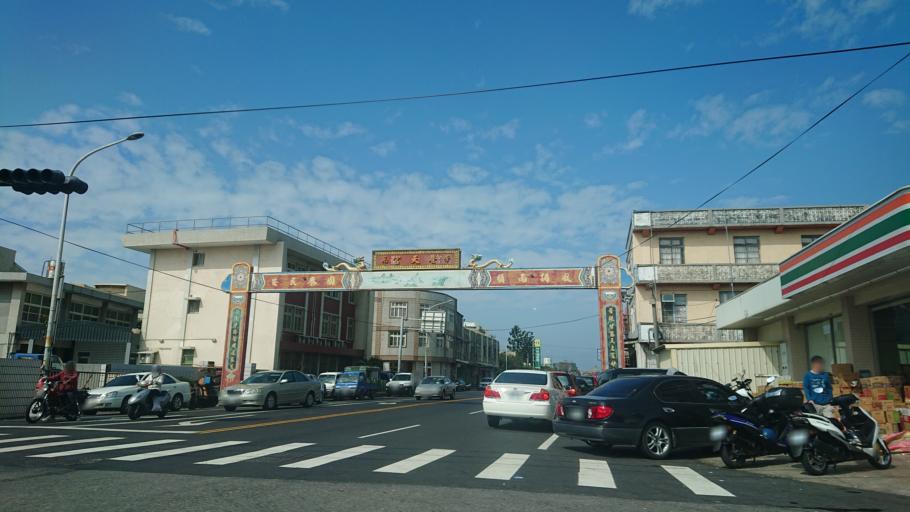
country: TW
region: Taiwan
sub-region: Changhua
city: Chang-hua
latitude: 23.9230
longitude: 120.3220
